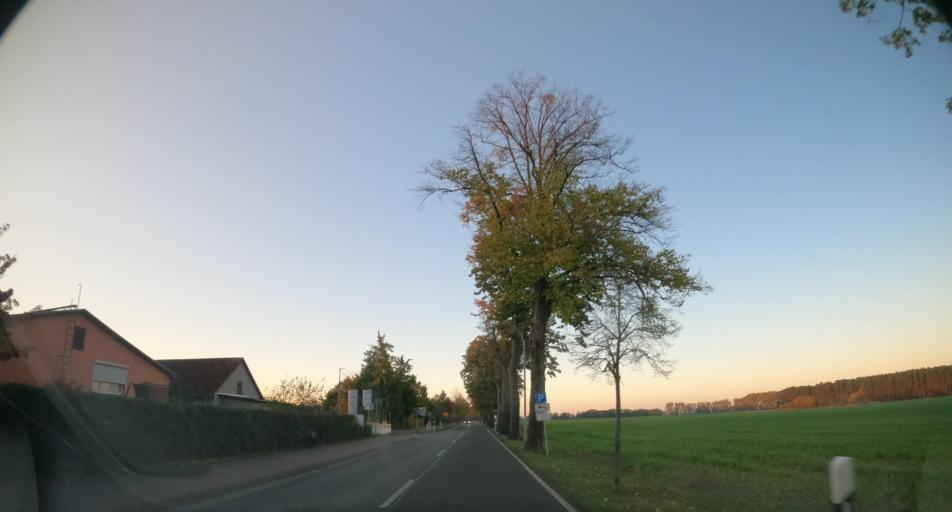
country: DE
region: Mecklenburg-Vorpommern
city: Ueckermunde
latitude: 53.7442
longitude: 14.0321
